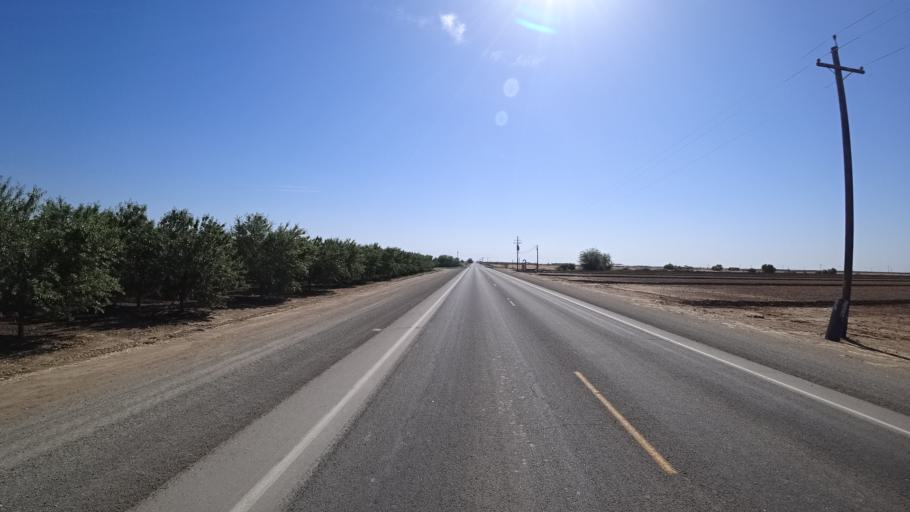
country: US
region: California
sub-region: Kings County
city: Home Garden
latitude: 36.2110
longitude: -119.5705
